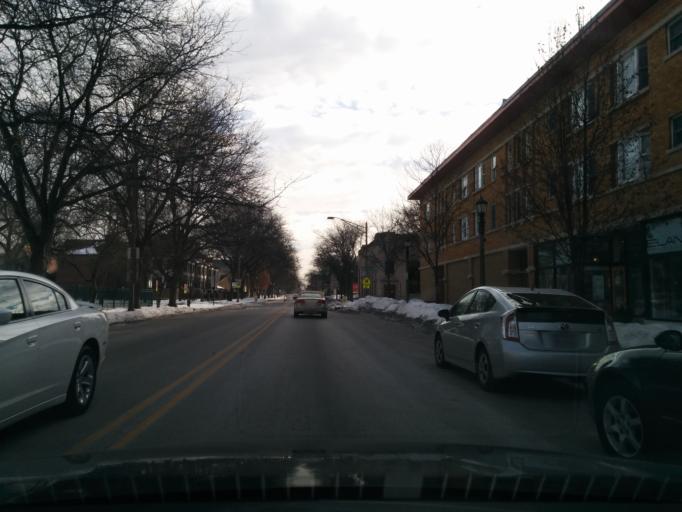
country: US
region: Illinois
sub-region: Cook County
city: Forest Park
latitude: 41.8883
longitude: -87.8187
